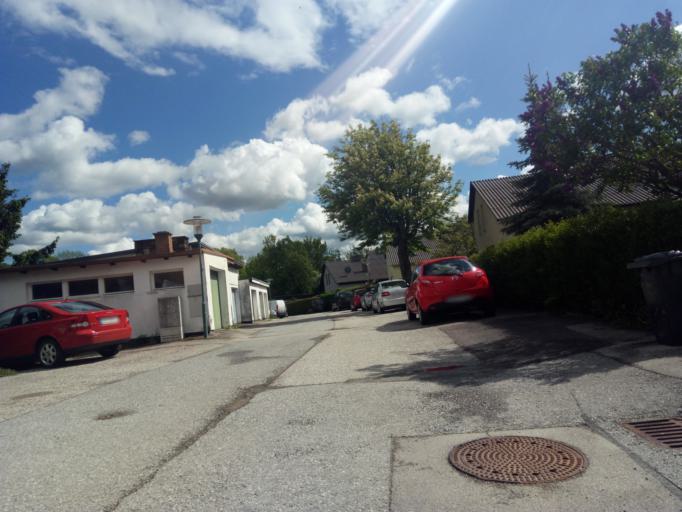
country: AT
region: Lower Austria
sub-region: Politischer Bezirk Modling
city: Breitenfurt bei Wien
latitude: 48.1376
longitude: 16.1380
